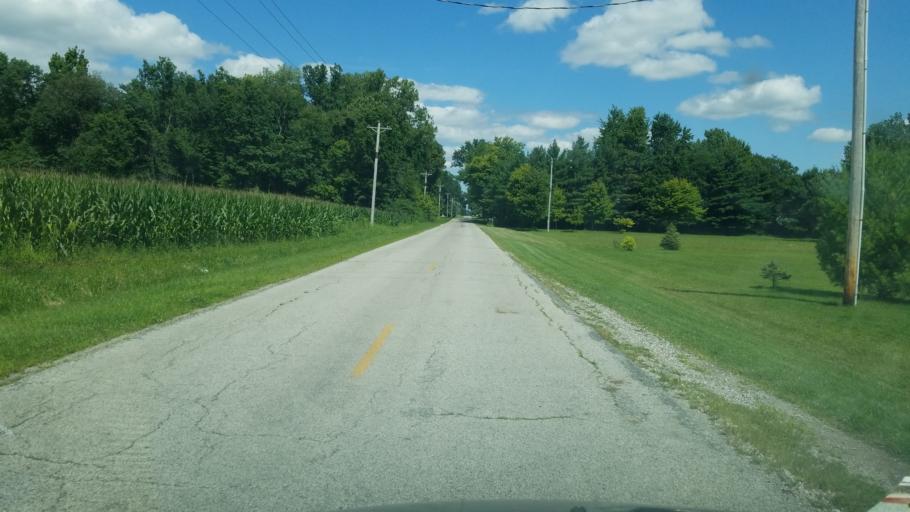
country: US
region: Ohio
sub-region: Henry County
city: Liberty Center
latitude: 41.4914
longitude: -83.9413
